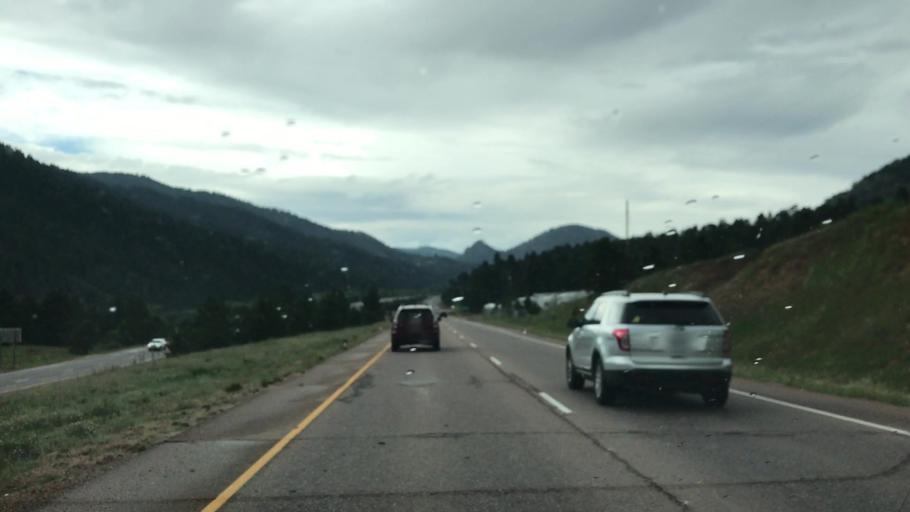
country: US
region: Colorado
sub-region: El Paso County
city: Cascade-Chipita Park
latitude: 38.9398
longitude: -105.0125
